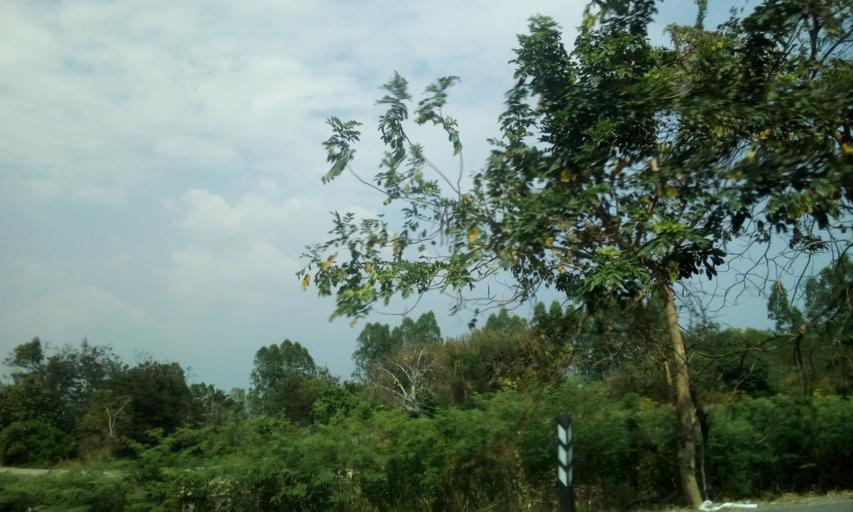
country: TH
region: Nakhon Nayok
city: Nakhon Nayok
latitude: 14.2074
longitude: 101.1840
